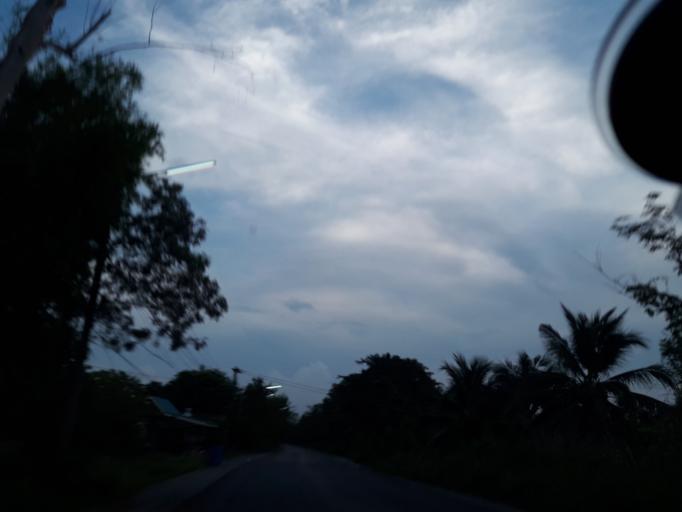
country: TH
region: Pathum Thani
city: Nong Suea
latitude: 14.1626
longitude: 100.8690
